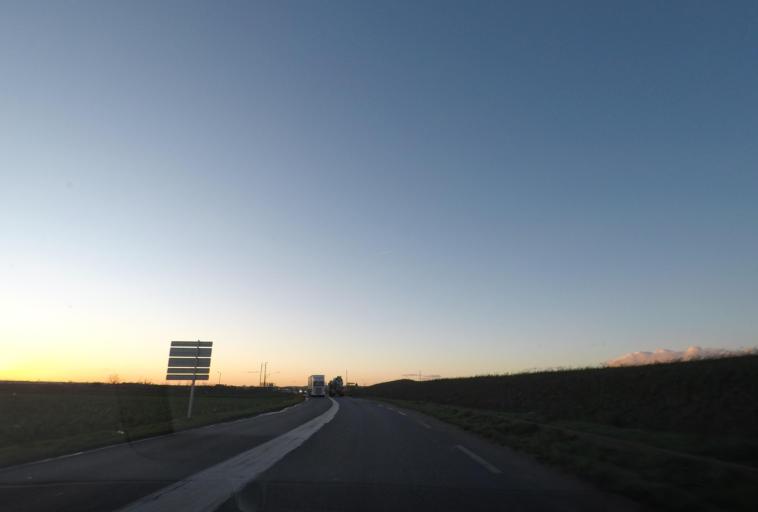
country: FR
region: Ile-de-France
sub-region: Departement de l'Essonne
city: Bondoufle
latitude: 48.6141
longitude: 2.3596
